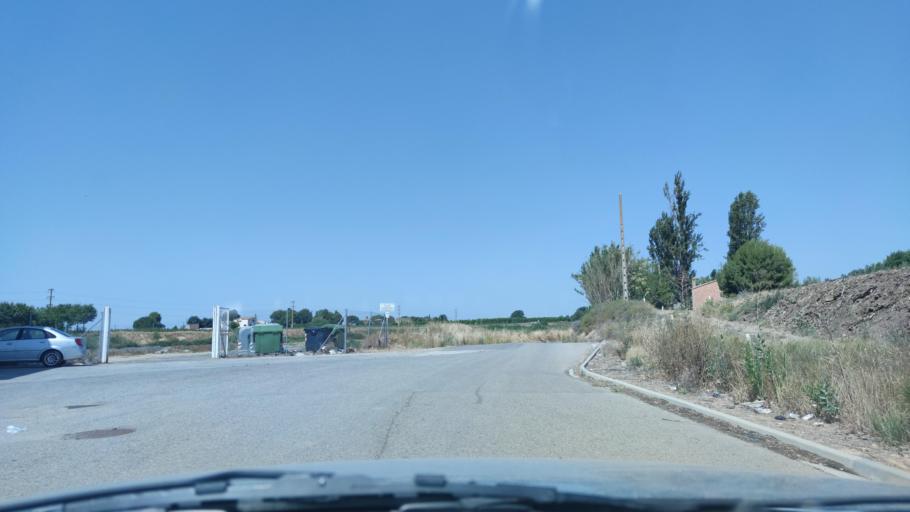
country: ES
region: Catalonia
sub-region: Provincia de Lleida
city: Torrefarrera
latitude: 41.6686
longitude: 0.5955
